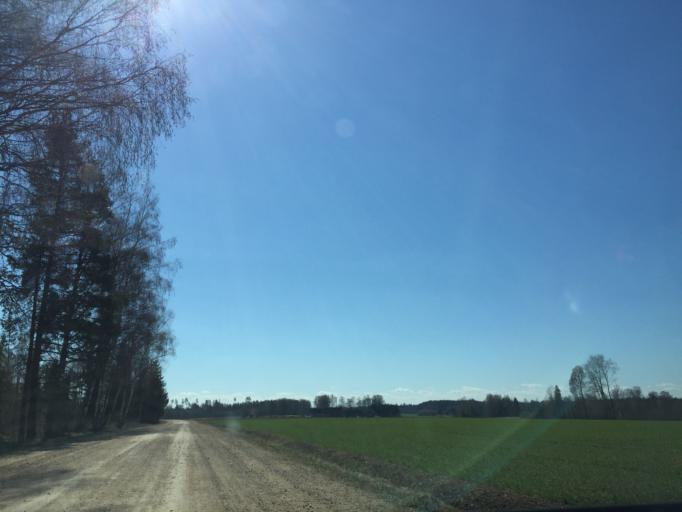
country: EE
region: Viljandimaa
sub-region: Viiratsi vald
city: Viiratsi
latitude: 58.3475
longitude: 25.7219
